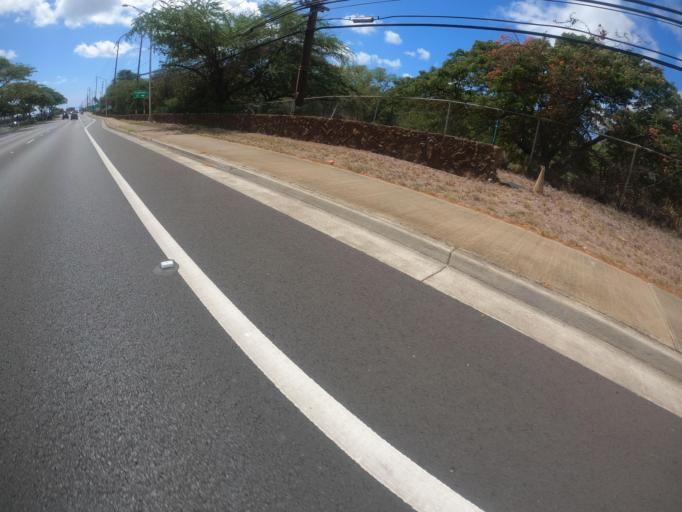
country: US
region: Hawaii
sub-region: Honolulu County
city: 'Ewa Gentry
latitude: 21.3514
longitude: -158.0280
